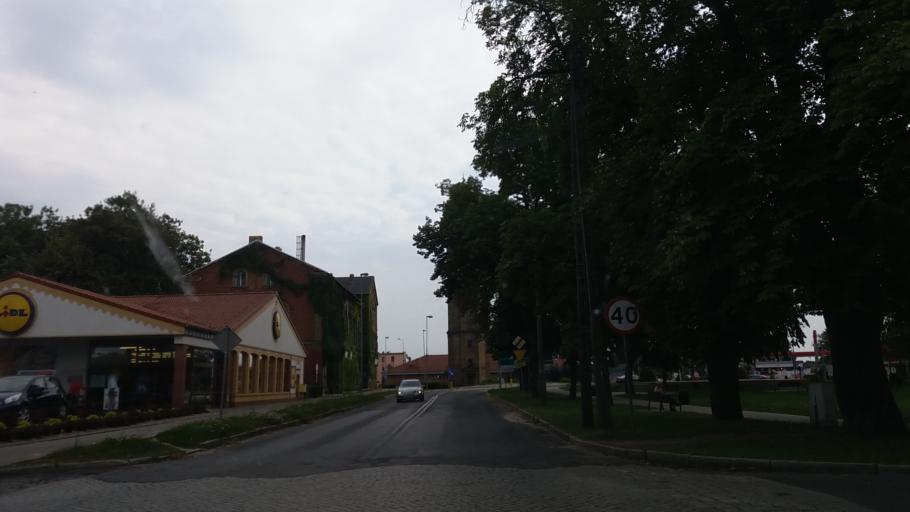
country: PL
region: Lubusz
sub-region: Powiat miedzyrzecki
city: Skwierzyna
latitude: 52.6000
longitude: 15.5056
